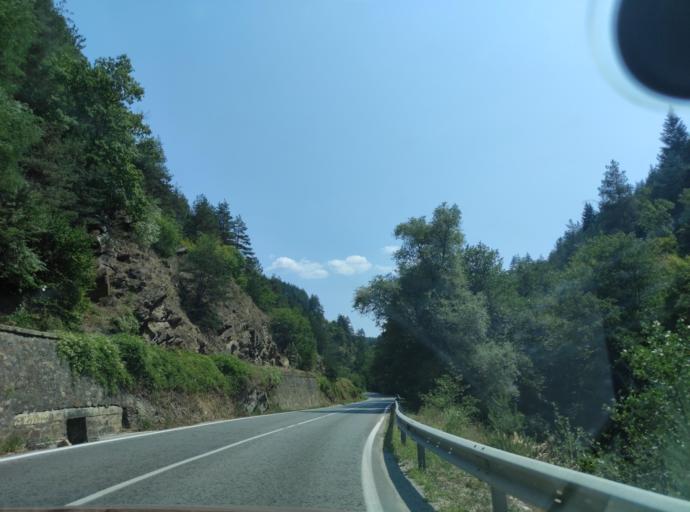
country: BG
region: Blagoevgrad
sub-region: Obshtina Belitsa
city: Belitsa
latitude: 41.8929
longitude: 23.5547
